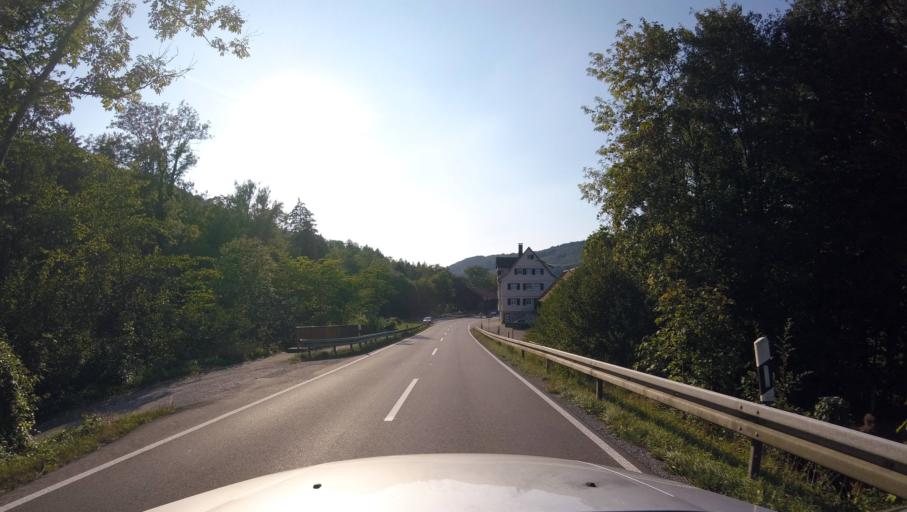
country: DE
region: Baden-Wuerttemberg
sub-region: Regierungsbezirk Stuttgart
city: Althutte
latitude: 48.8953
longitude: 9.5842
